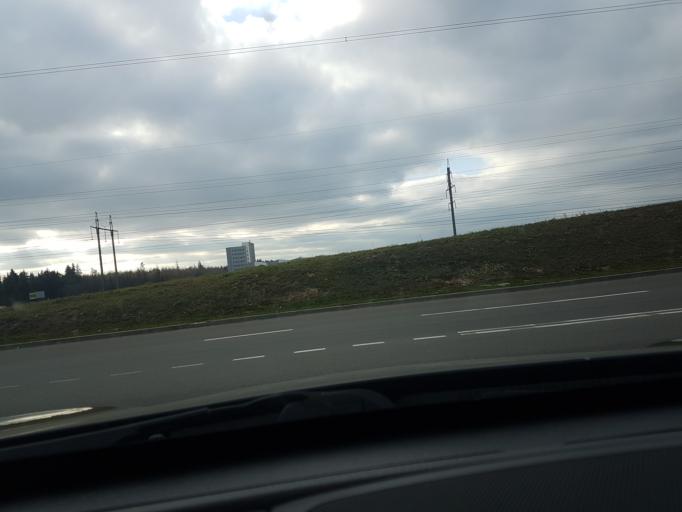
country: BY
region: Minsk
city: Malinovka
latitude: 53.8485
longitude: 27.4329
